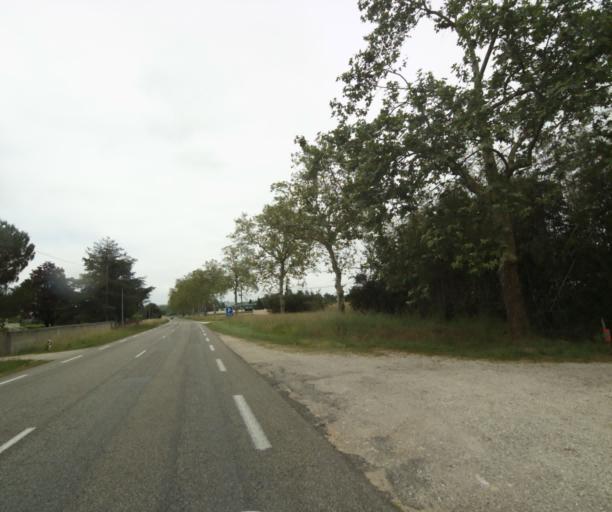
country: FR
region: Midi-Pyrenees
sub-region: Departement du Tarn-et-Garonne
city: Saint-Nauphary
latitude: 43.9756
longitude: 1.4081
